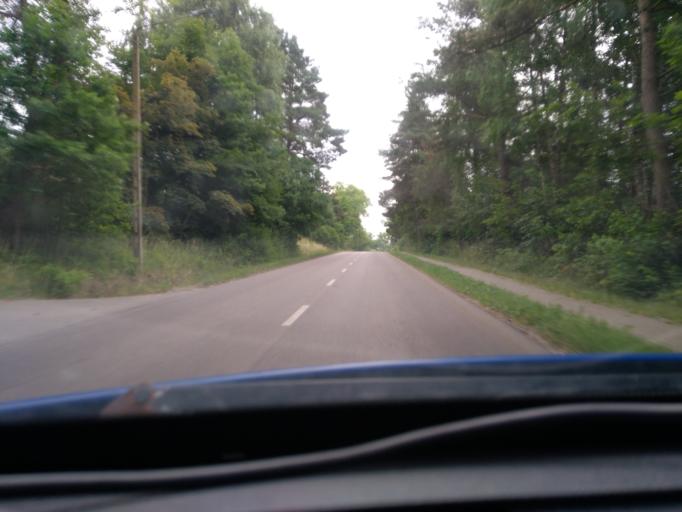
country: PL
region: Pomeranian Voivodeship
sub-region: Powiat kartuski
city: Przodkowo
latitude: 54.3606
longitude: 18.2631
